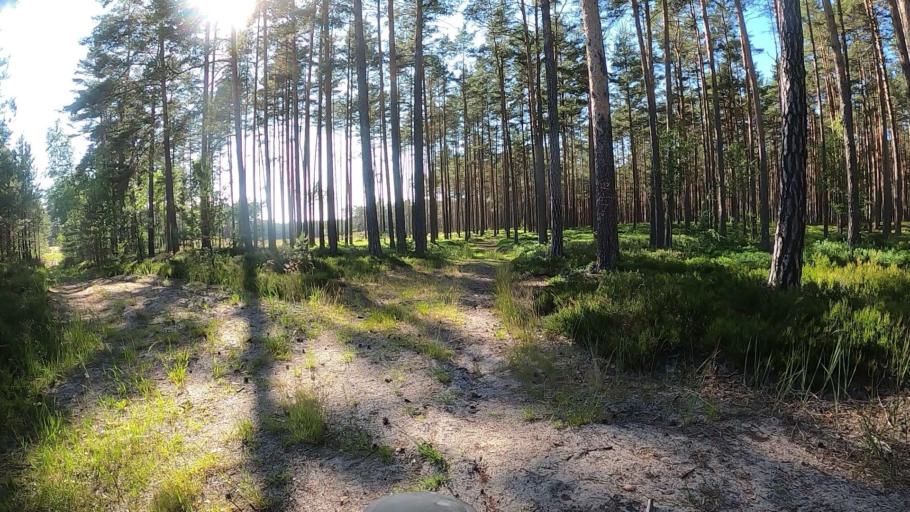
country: LV
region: Carnikava
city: Carnikava
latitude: 57.0977
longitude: 24.2354
